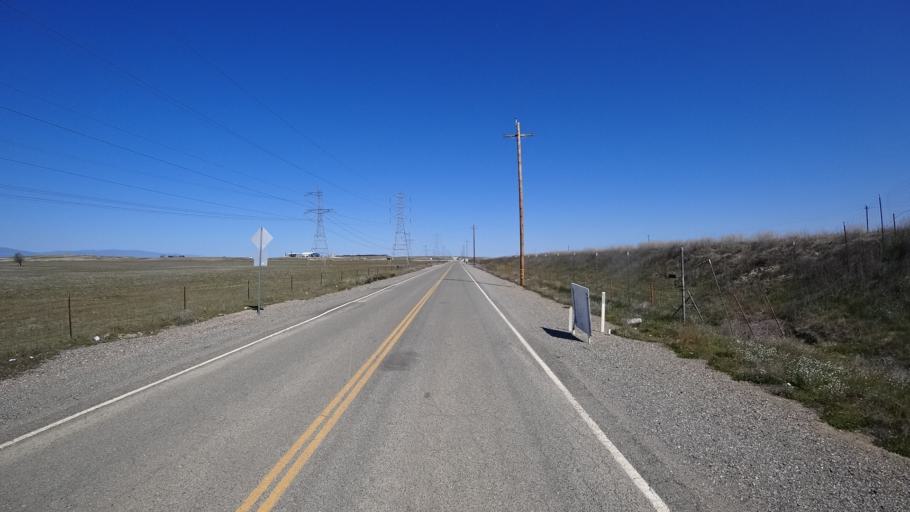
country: US
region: California
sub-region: Glenn County
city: Willows
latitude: 39.6263
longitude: -122.2729
